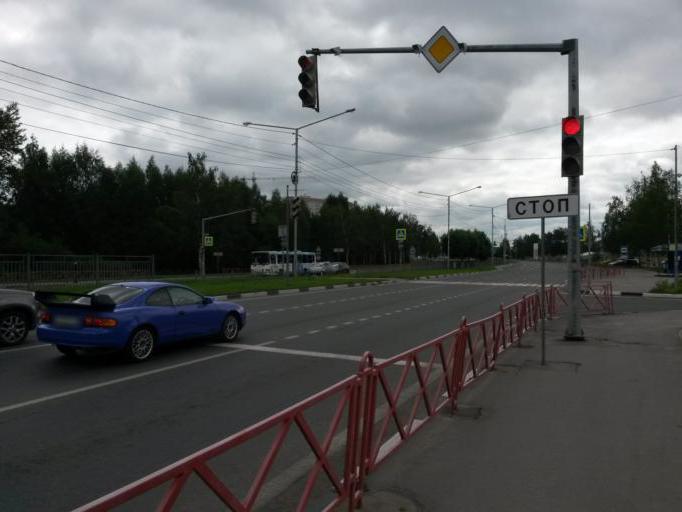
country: RU
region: Jaroslavl
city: Yaroslavl
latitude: 57.5910
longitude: 39.9016
